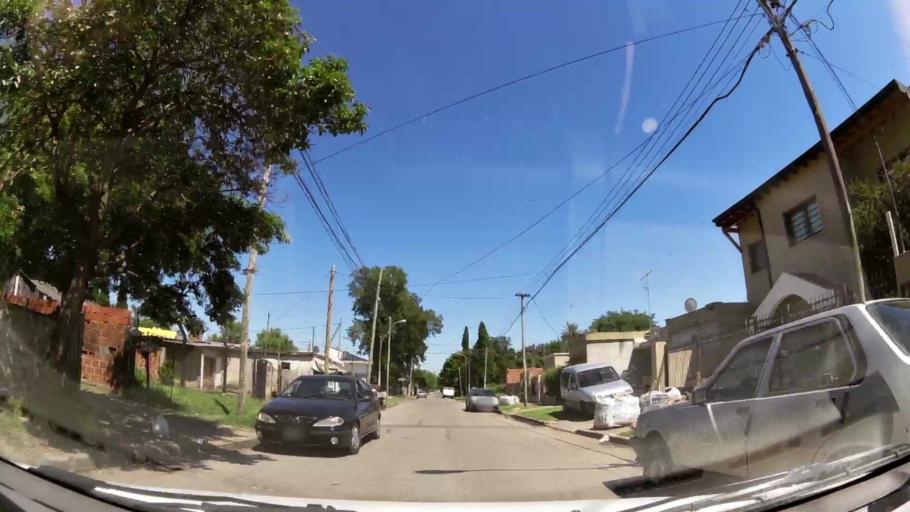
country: AR
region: Buenos Aires
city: Ituzaingo
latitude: -34.6811
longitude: -58.6580
